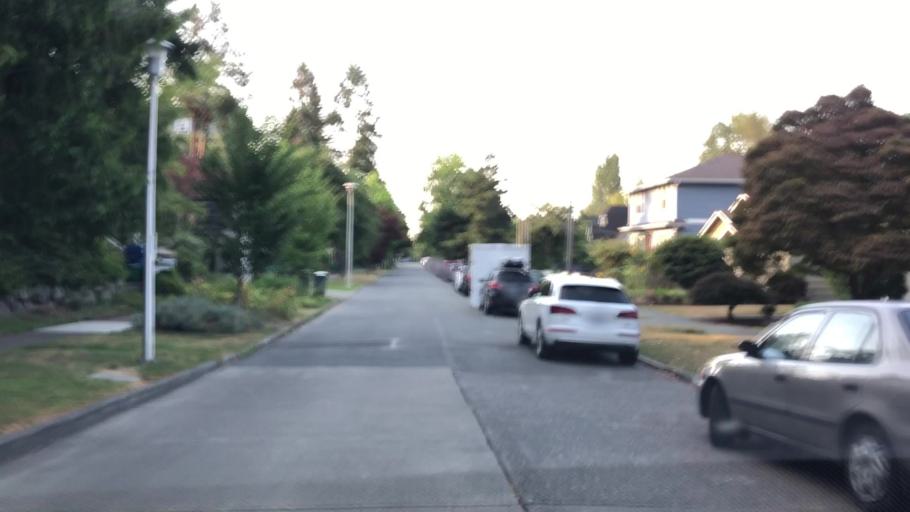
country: US
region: Washington
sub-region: King County
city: Yarrow Point
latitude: 47.6609
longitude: -122.2828
